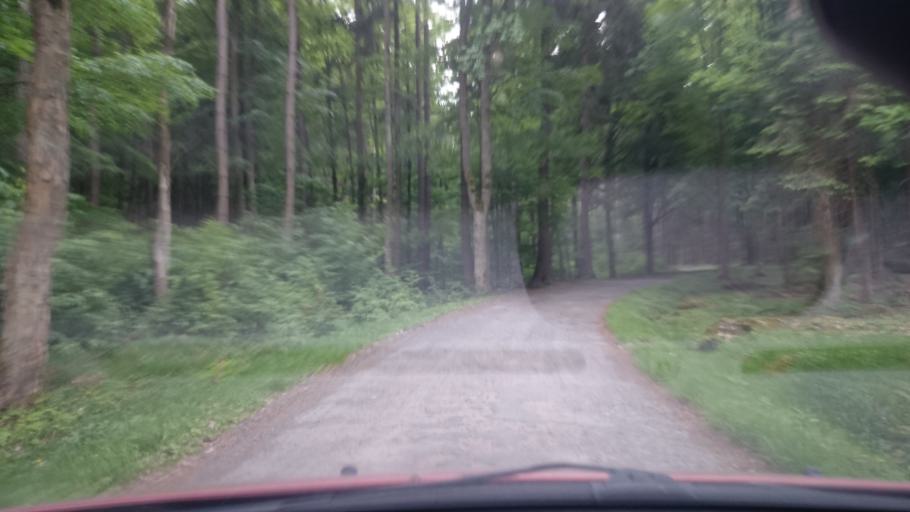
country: PL
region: Lower Silesian Voivodeship
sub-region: Powiat klodzki
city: Polanica-Zdroj
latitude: 50.3007
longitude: 16.5224
